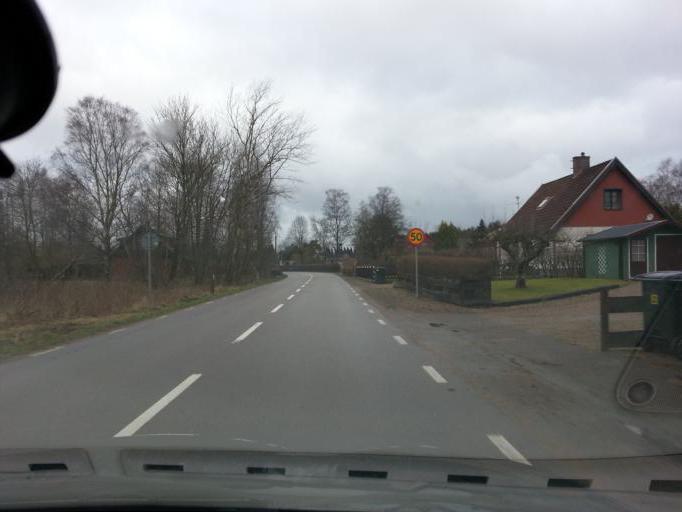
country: SE
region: Skane
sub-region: Klippans Kommun
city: Klippan
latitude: 56.0948
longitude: 13.1452
